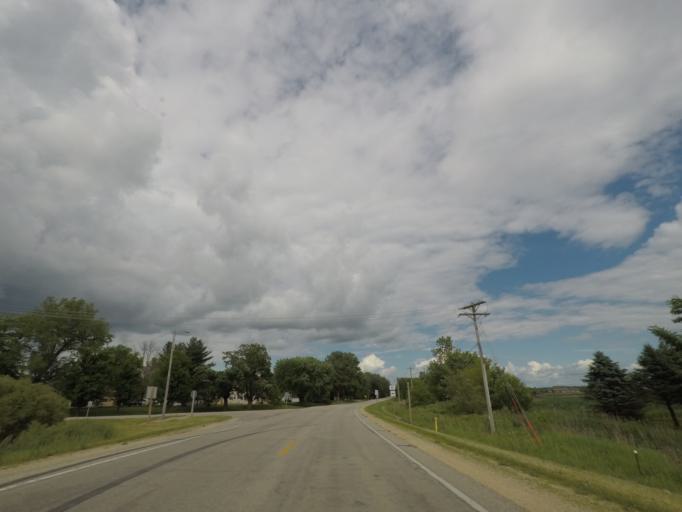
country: US
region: Wisconsin
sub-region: Dane County
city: Belleville
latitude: 42.8279
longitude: -89.5070
